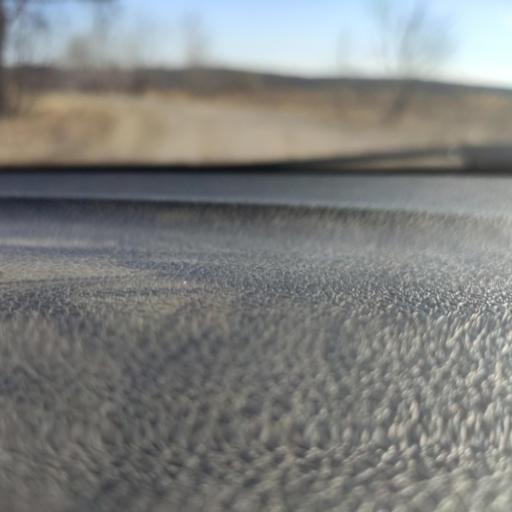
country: RU
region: Bashkortostan
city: Blagoveshchensk
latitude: 54.9091
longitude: 56.0969
